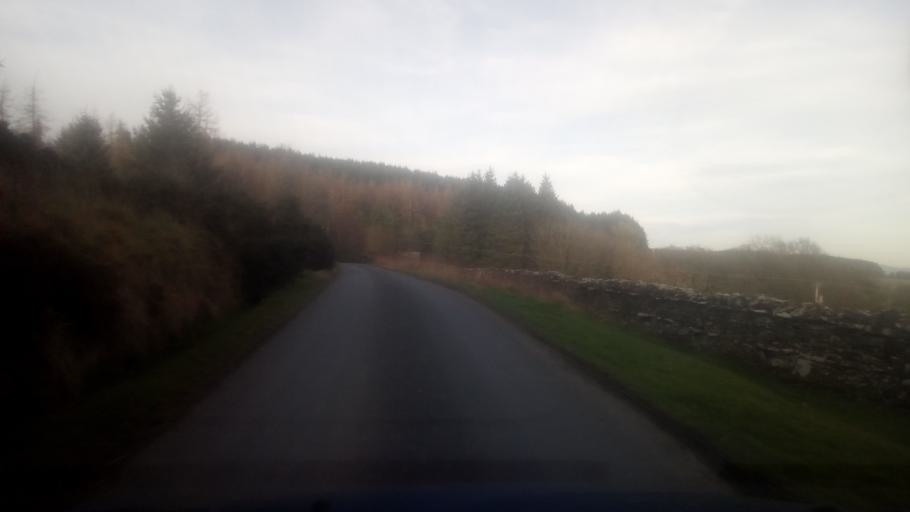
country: GB
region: Scotland
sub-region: The Scottish Borders
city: Jedburgh
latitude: 55.3939
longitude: -2.5657
